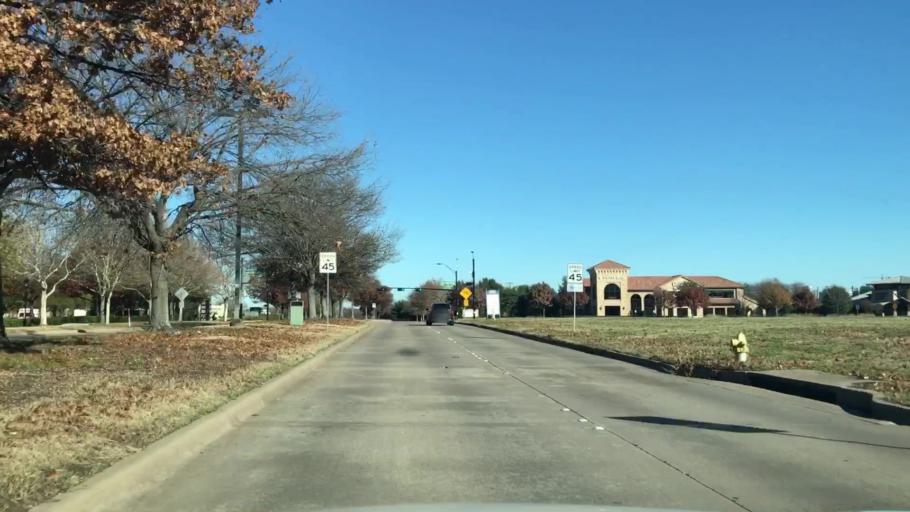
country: US
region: Texas
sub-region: Denton County
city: The Colony
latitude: 33.0885
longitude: -96.8392
